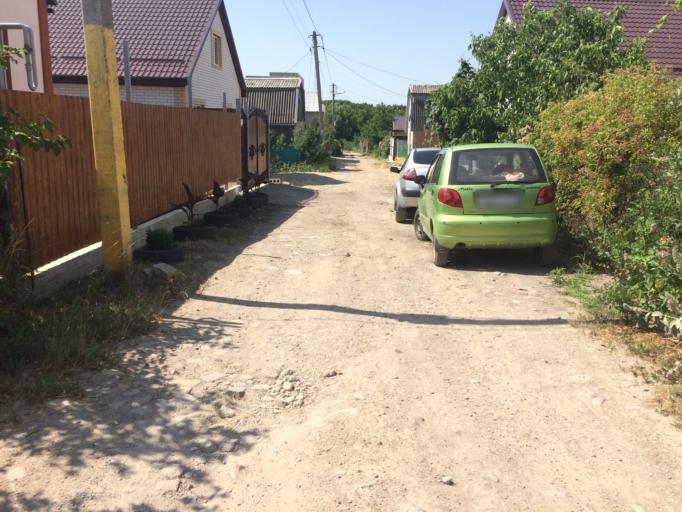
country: RU
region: Stavropol'skiy
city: Tatarka
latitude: 44.9814
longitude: 41.9409
